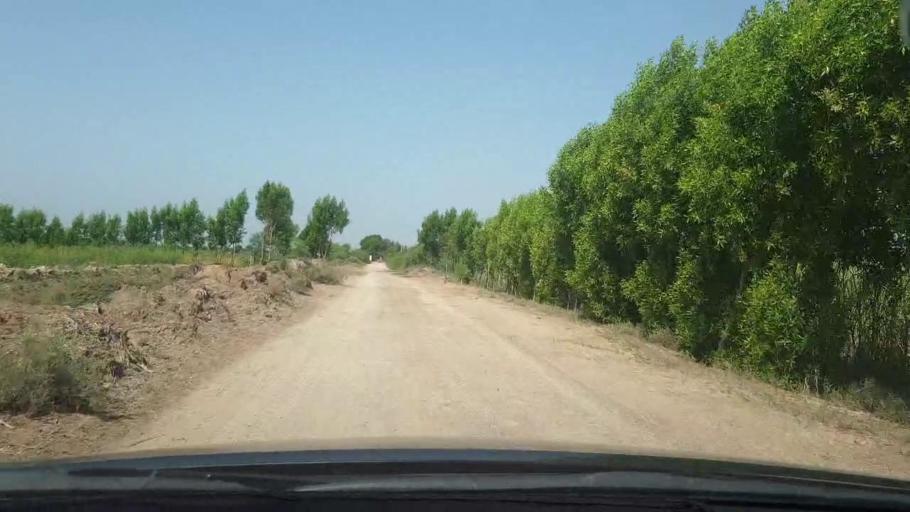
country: PK
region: Sindh
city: Tando Bago
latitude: 24.7194
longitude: 69.0981
